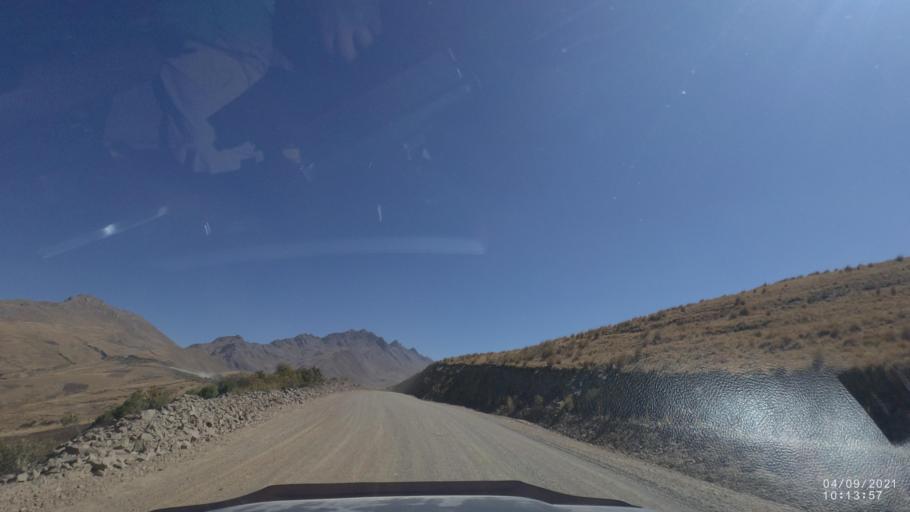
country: BO
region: Cochabamba
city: Sipe Sipe
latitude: -17.3333
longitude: -66.4058
